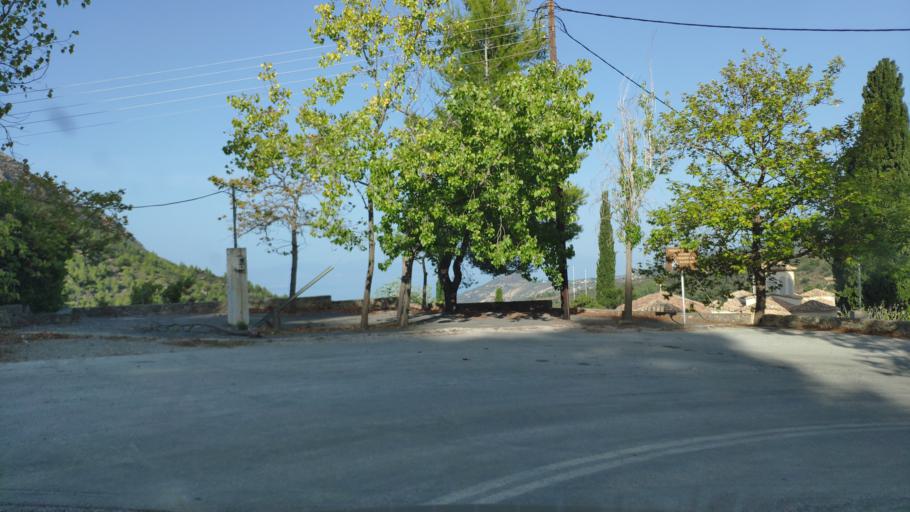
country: GR
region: West Greece
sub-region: Nomos Achaias
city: Aiyira
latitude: 38.0710
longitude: 22.3926
